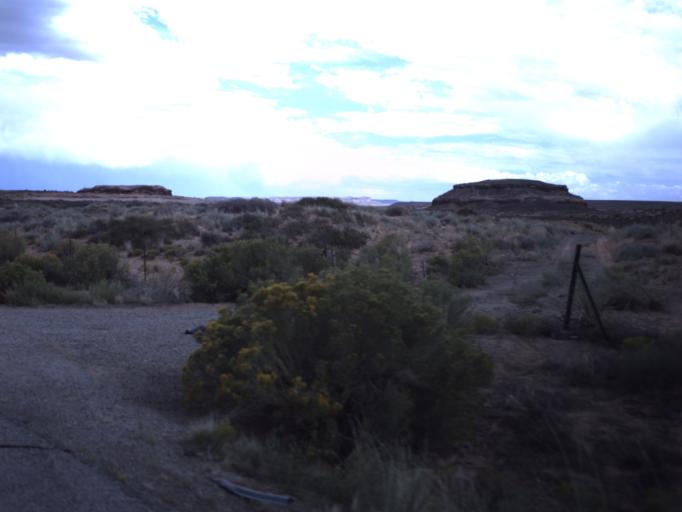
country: US
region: Utah
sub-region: San Juan County
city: Blanding
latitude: 37.2983
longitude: -109.4655
